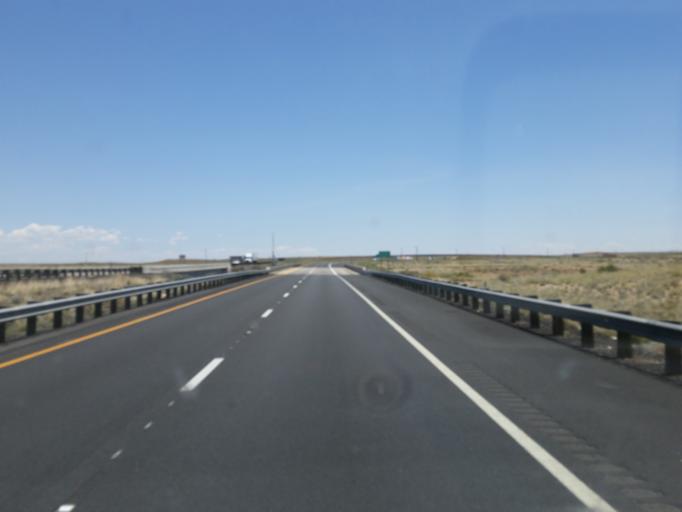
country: US
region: Arizona
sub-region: Coconino County
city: LeChee
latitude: 35.1172
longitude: -111.1012
